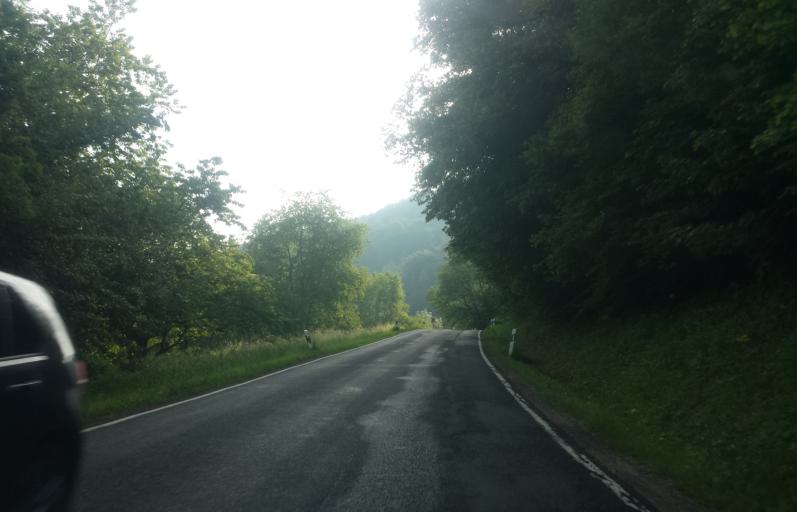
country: DE
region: Bavaria
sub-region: Upper Franconia
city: Ebermannstadt
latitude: 49.7868
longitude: 11.2042
